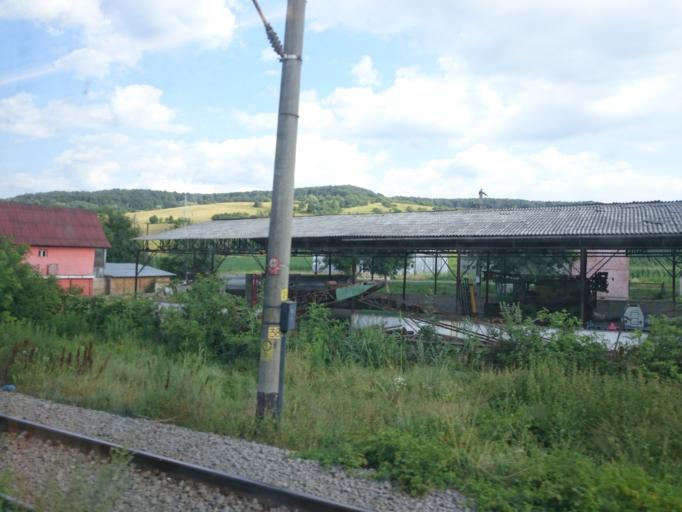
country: RO
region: Sibiu
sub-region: Oras Dumbraveni
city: Dumbraveni
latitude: 46.2156
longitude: 24.5602
